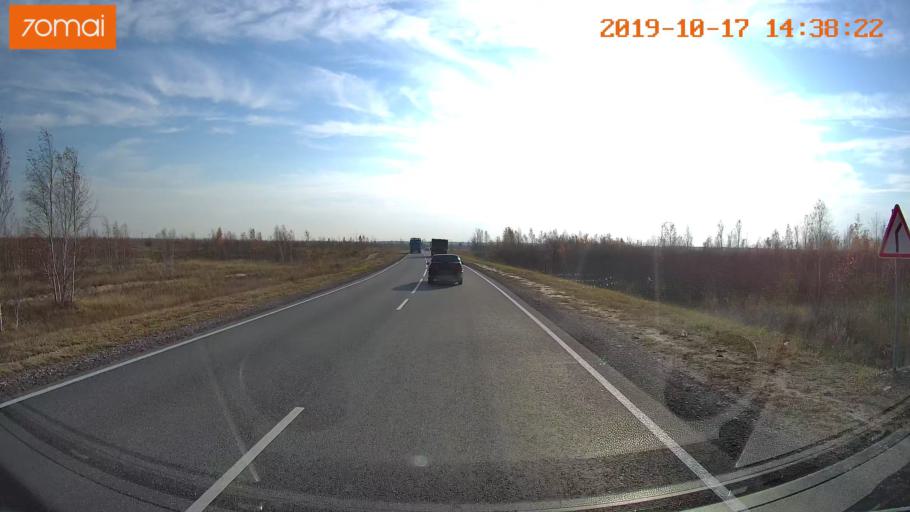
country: RU
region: Rjazan
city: Solotcha
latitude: 54.8712
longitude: 39.9849
